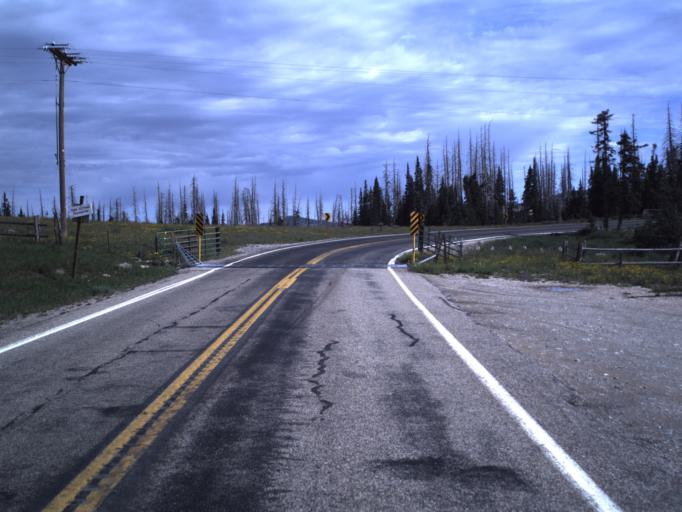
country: US
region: Utah
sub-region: Iron County
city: Cedar City
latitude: 37.6048
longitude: -112.8509
